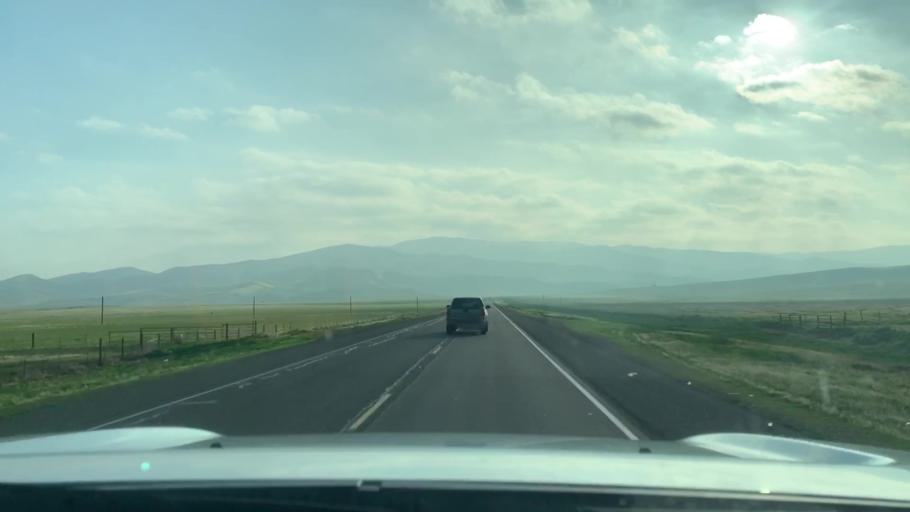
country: US
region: California
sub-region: Kings County
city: Avenal
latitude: 35.8038
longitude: -120.1046
